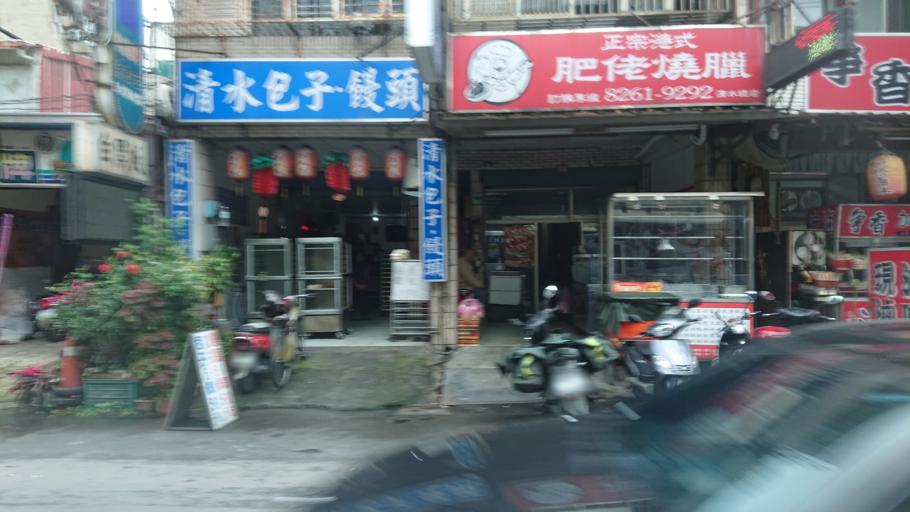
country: TW
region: Taipei
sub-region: Taipei
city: Banqiao
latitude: 24.9818
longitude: 121.4602
